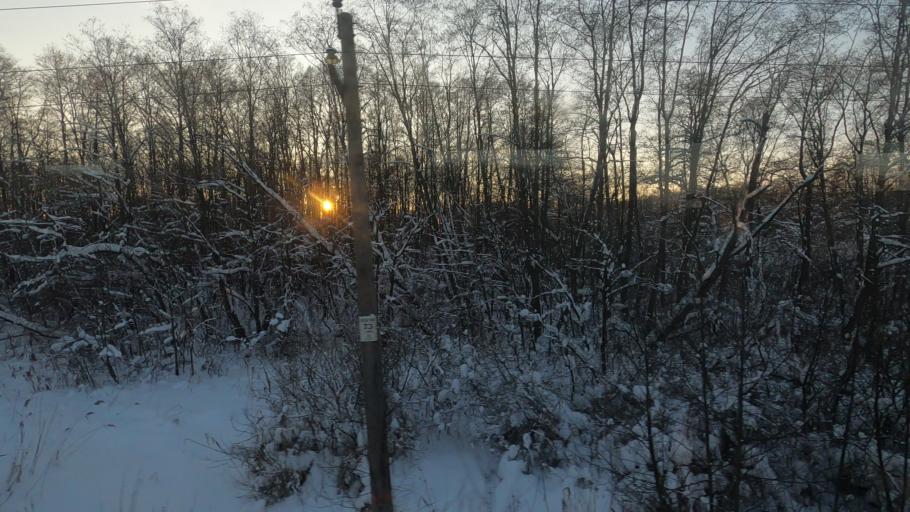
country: RU
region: Moskovskaya
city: Dmitrov
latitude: 56.3874
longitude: 37.5108
